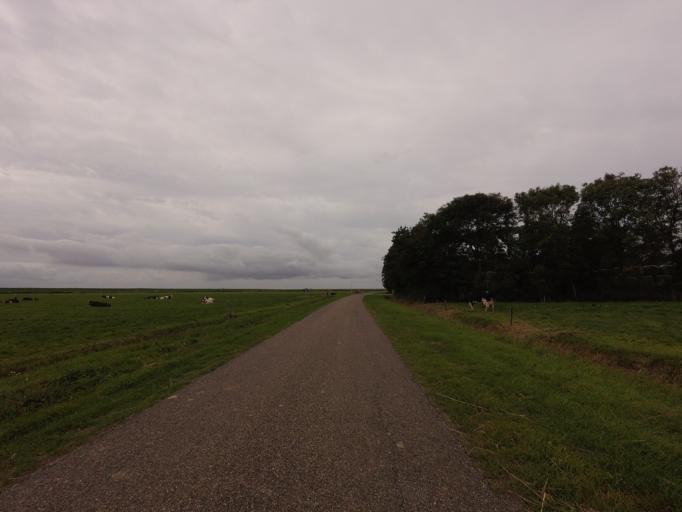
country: NL
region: Friesland
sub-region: Gemeente Ameland
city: Hollum
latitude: 53.4320
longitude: 5.6964
